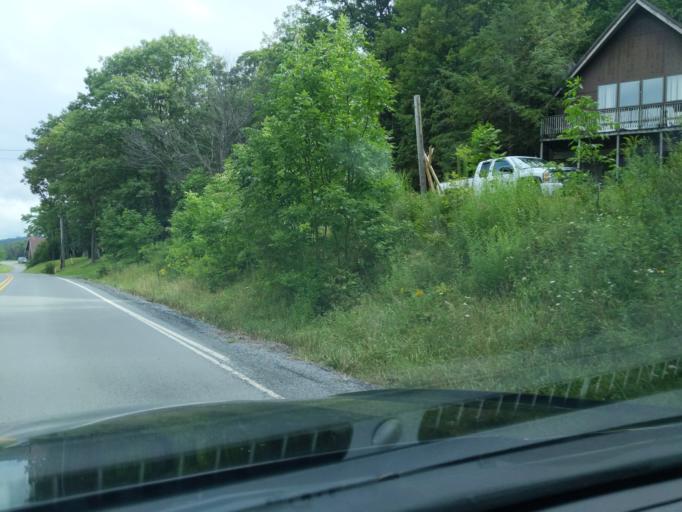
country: US
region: Pennsylvania
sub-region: Cambria County
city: Beaverdale
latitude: 40.2980
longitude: -78.5780
